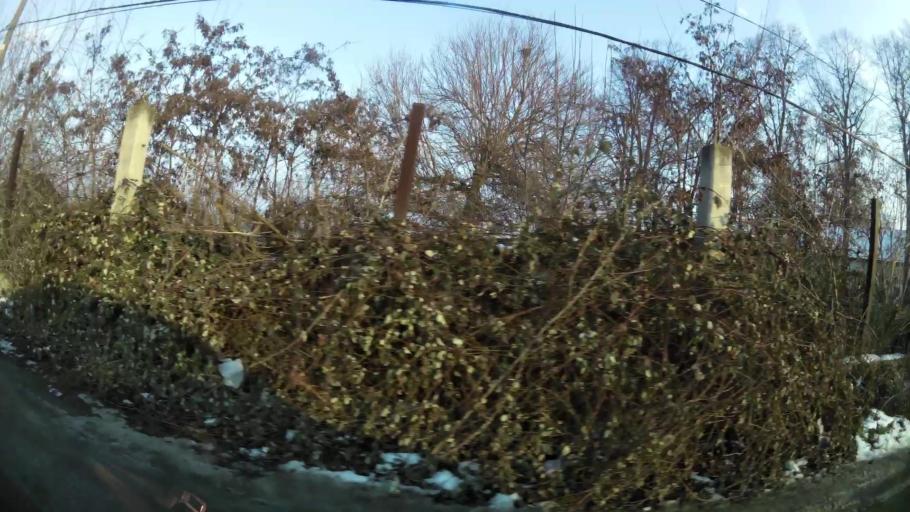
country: MK
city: Creshevo
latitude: 42.0159
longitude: 21.5234
